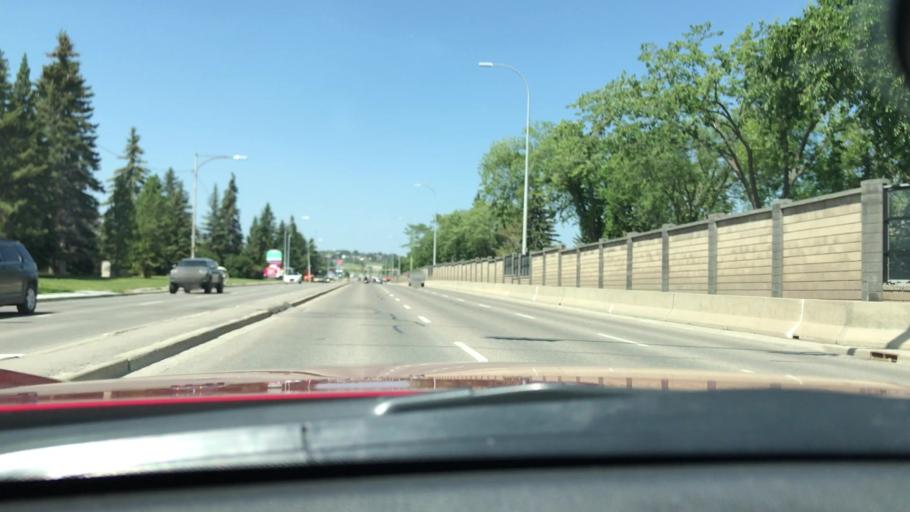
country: CA
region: Alberta
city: Calgary
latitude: 51.0470
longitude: -114.1470
